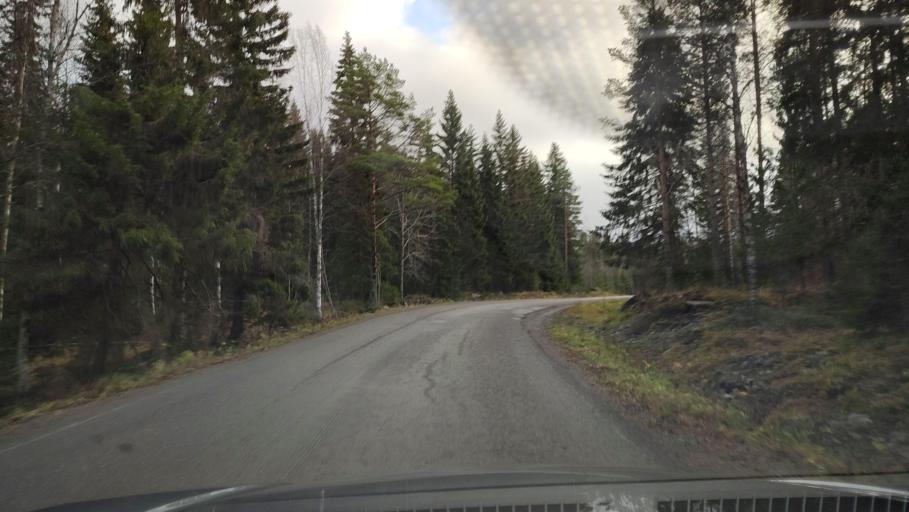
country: FI
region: Ostrobothnia
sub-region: Sydosterbotten
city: Kristinestad
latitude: 62.1526
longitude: 21.5365
